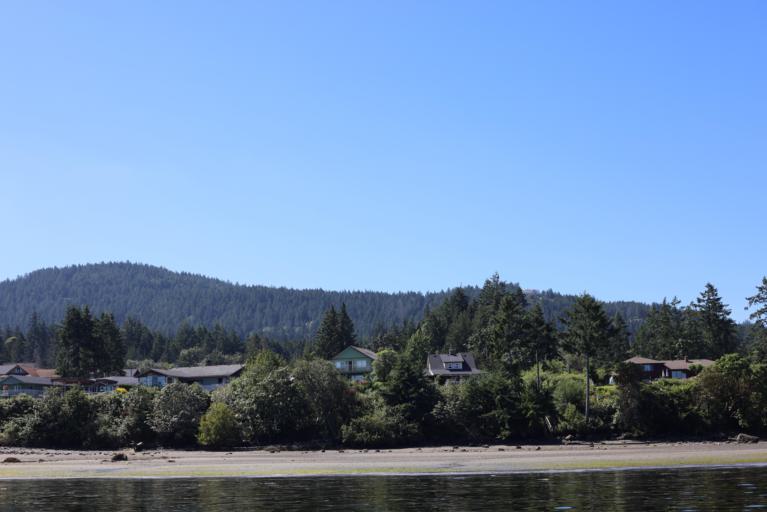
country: CA
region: British Columbia
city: North Cowichan
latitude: 48.8646
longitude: -123.6314
